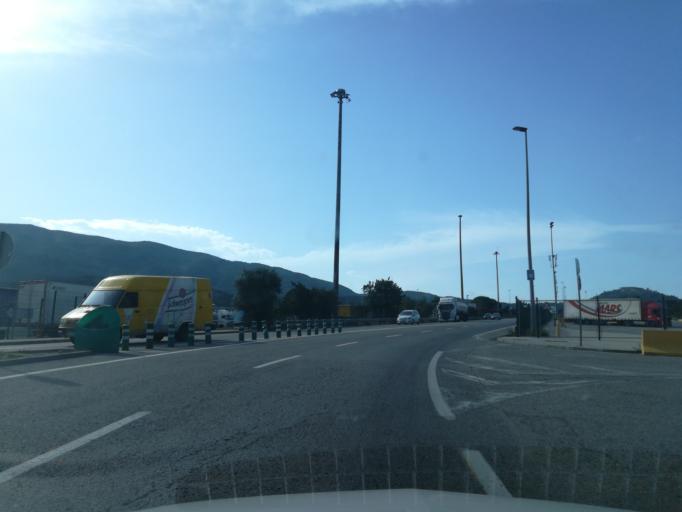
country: ES
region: Catalonia
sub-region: Provincia de Girona
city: la Jonquera
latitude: 42.4308
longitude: 2.8672
